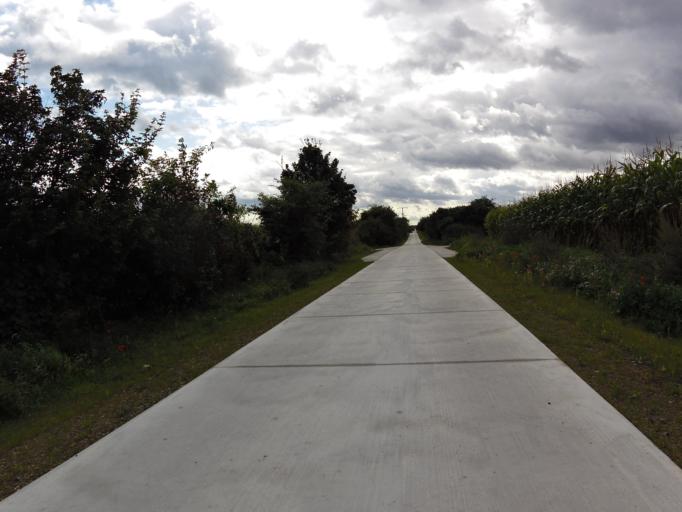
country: DE
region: Saxony-Anhalt
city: Arneburg
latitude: 52.6644
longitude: 12.0044
